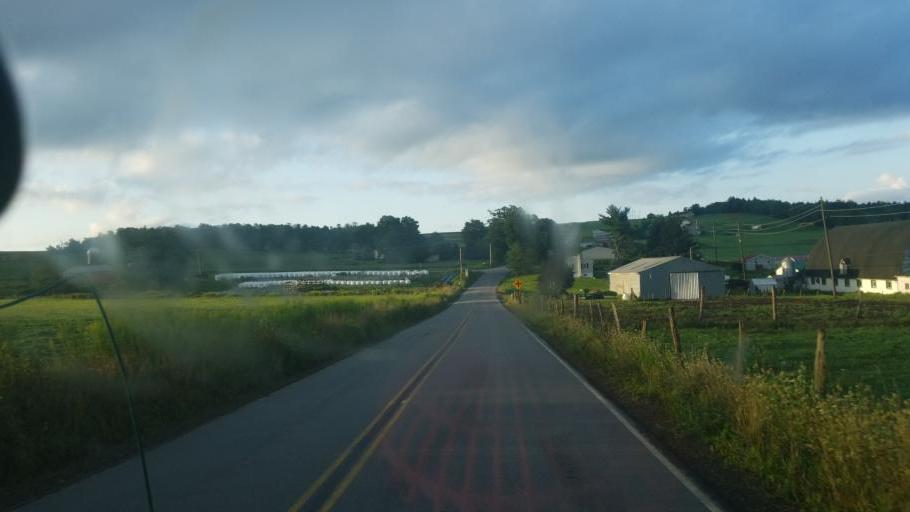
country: US
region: Pennsylvania
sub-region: Potter County
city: Galeton
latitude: 41.8887
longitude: -77.7615
